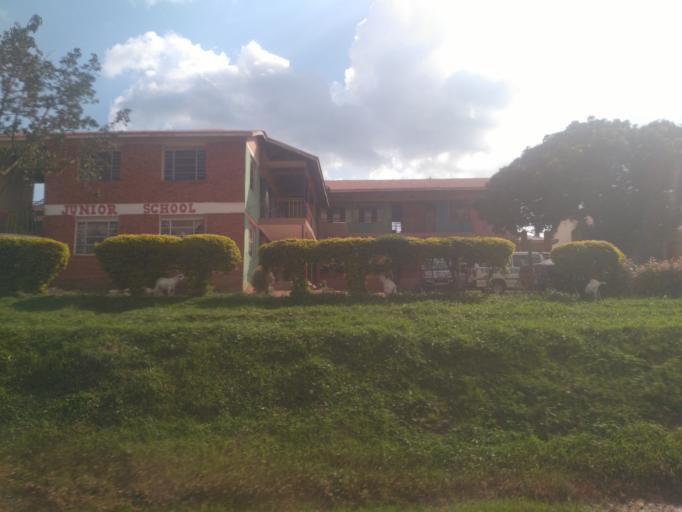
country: UG
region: Central Region
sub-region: Wakiso District
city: Kajansi
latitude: 0.2791
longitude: 32.4729
